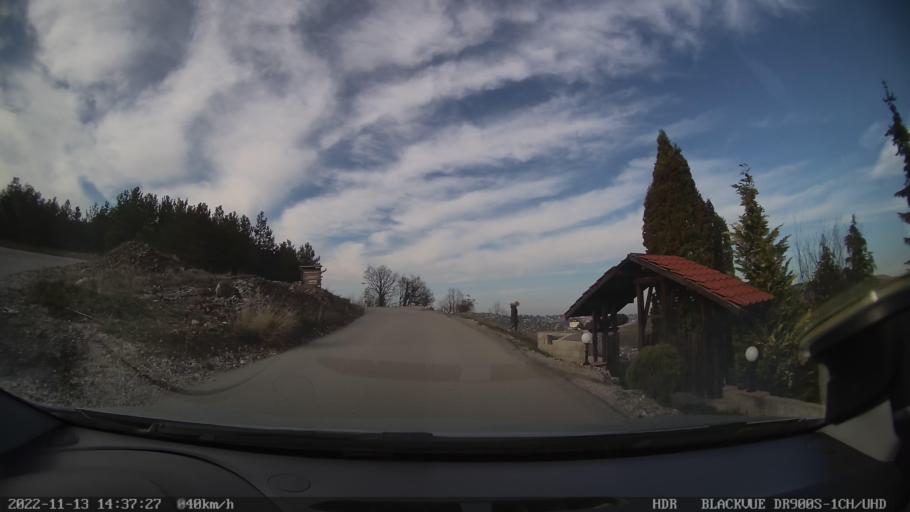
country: RS
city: Zlatibor
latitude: 43.7113
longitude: 19.7161
